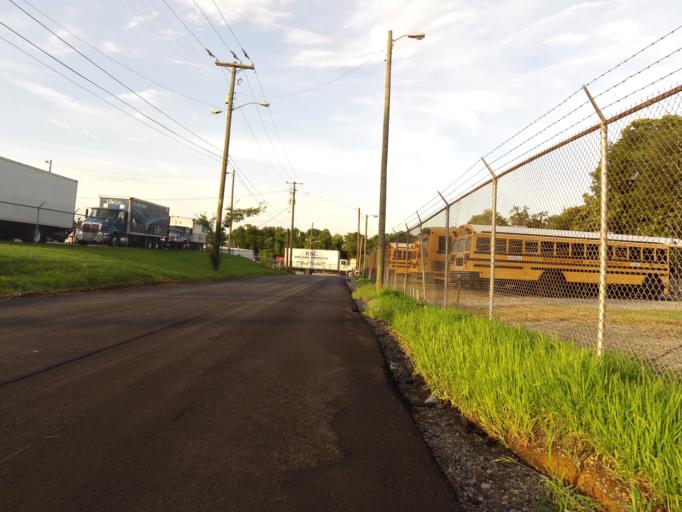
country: US
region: Tennessee
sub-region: Knox County
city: Knoxville
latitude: 35.9756
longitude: -83.9329
